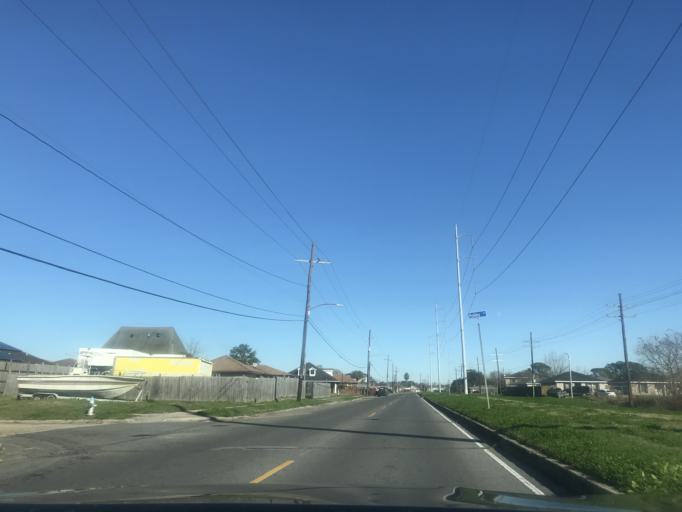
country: US
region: Louisiana
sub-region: Saint Bernard Parish
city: Arabi
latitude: 30.0226
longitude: -89.9977
